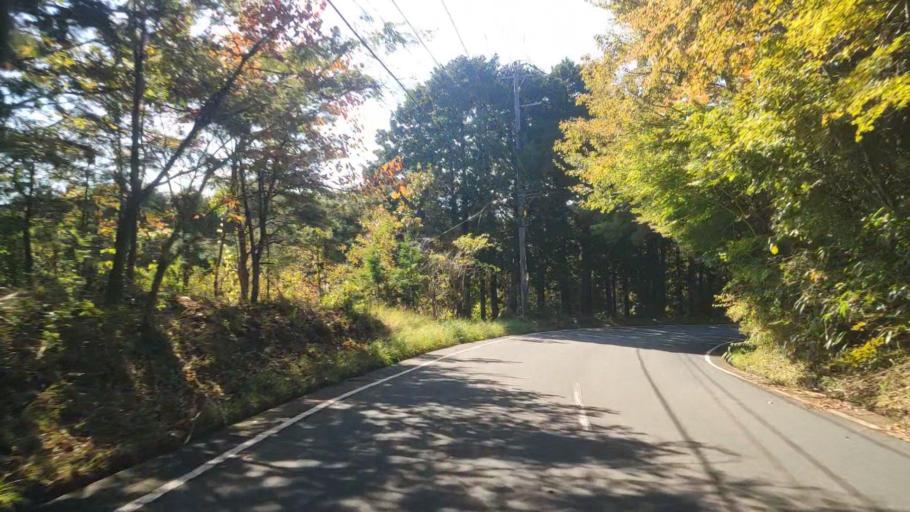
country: JP
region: Shizuoka
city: Atami
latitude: 35.0312
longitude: 139.0129
